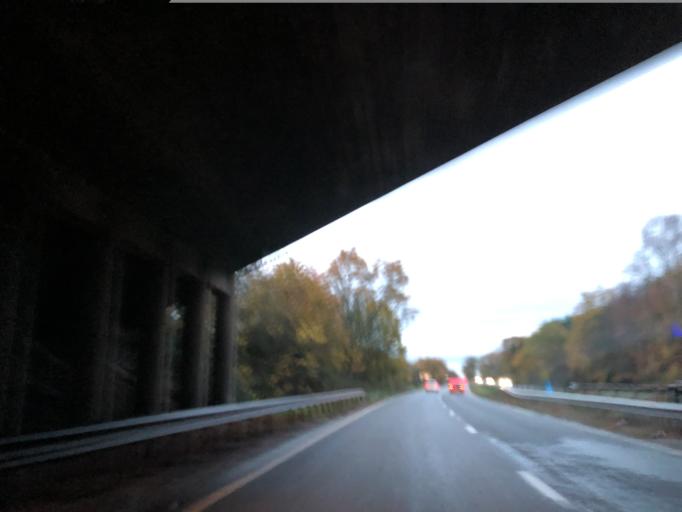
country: GB
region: England
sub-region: Solihull
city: Bickenhill
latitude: 52.4590
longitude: -1.7023
